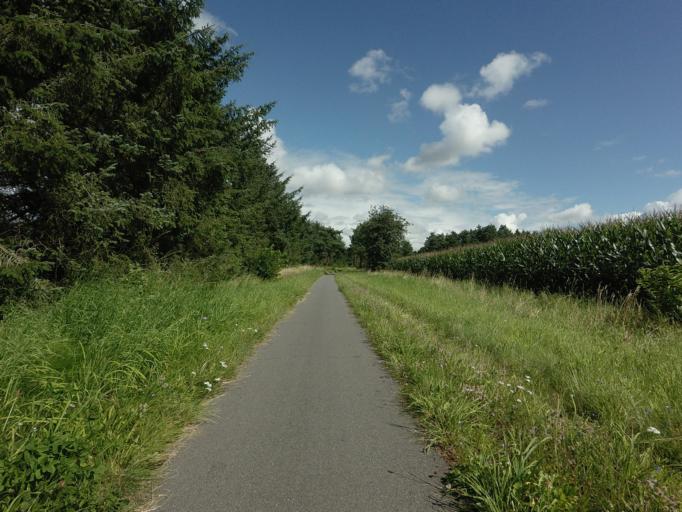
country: DK
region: Central Jutland
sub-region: Silkeborg Kommune
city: Svejbaek
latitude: 56.2087
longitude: 9.6720
